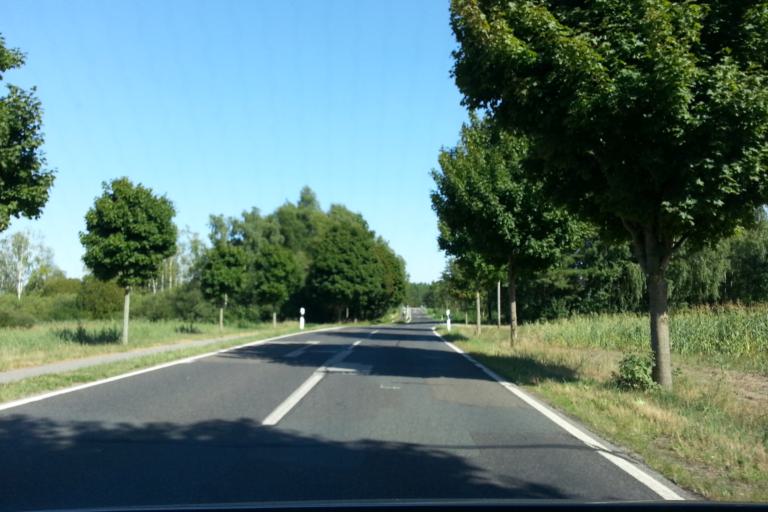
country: DE
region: Mecklenburg-Vorpommern
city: Eggesin
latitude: 53.6810
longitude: 14.0421
